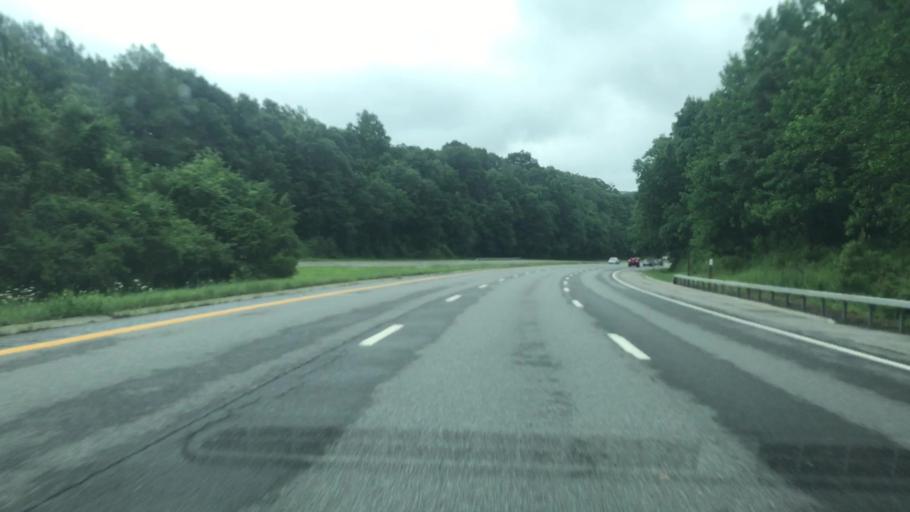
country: US
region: New York
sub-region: Westchester County
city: Briarcliff Manor
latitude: 41.1914
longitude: -73.8063
